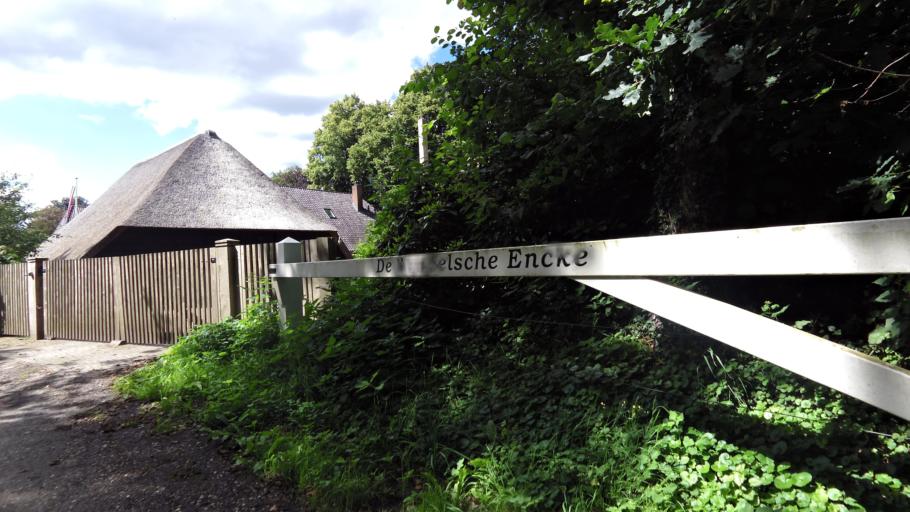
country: NL
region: Gelderland
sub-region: Gemeente Epe
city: Vaassen
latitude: 52.2569
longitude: 5.9383
